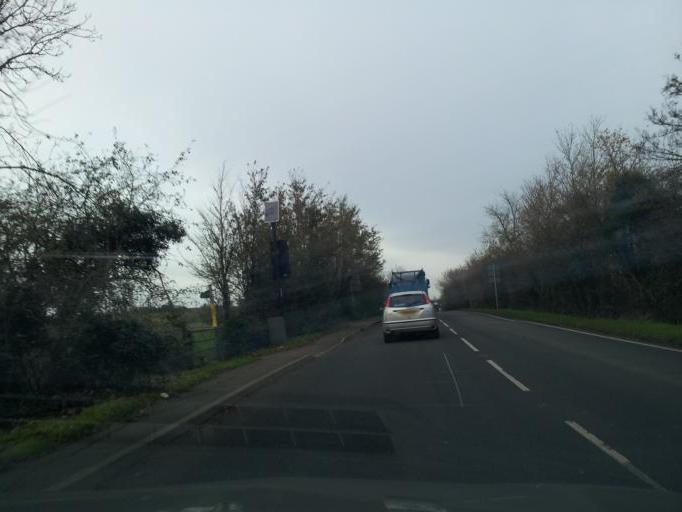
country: GB
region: England
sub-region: Buckinghamshire
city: Aylesbury
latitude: 51.8551
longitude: -0.7670
